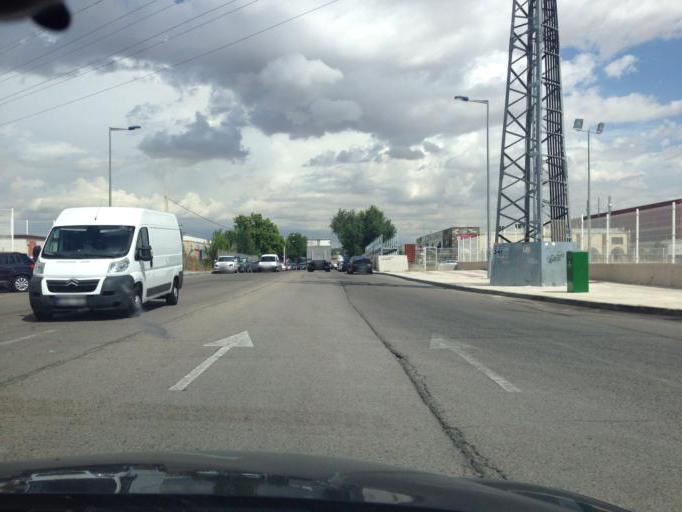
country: ES
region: Madrid
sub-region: Provincia de Madrid
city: San Fernando de Henares
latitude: 40.4481
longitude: -3.5059
